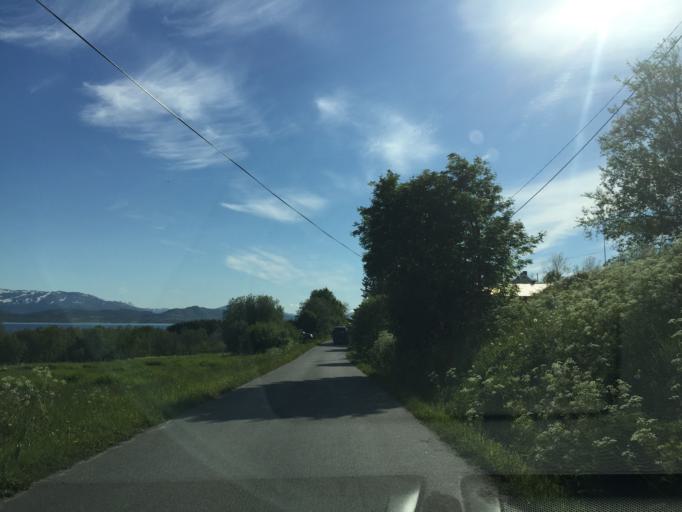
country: NO
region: Nordland
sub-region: Bodo
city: Loding
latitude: 67.2844
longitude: 14.6073
